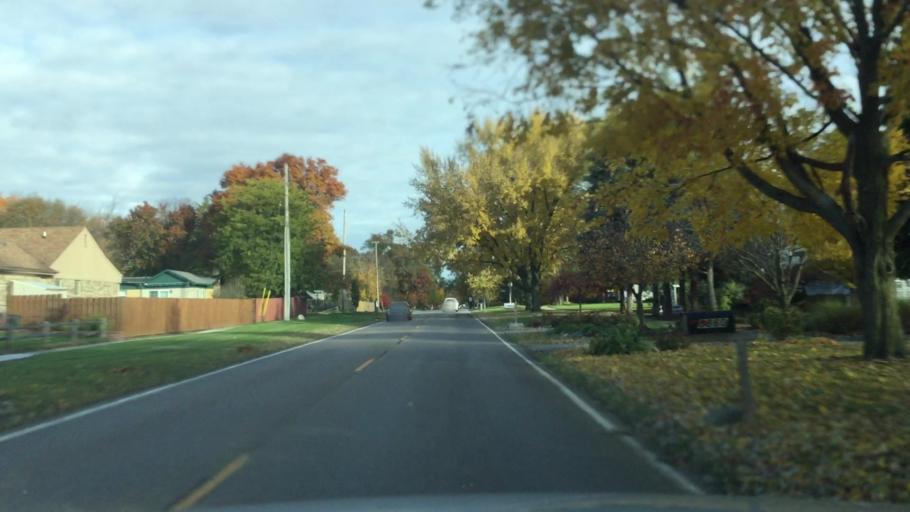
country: US
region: Michigan
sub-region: Wayne County
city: Westland
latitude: 42.3538
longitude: -83.4205
